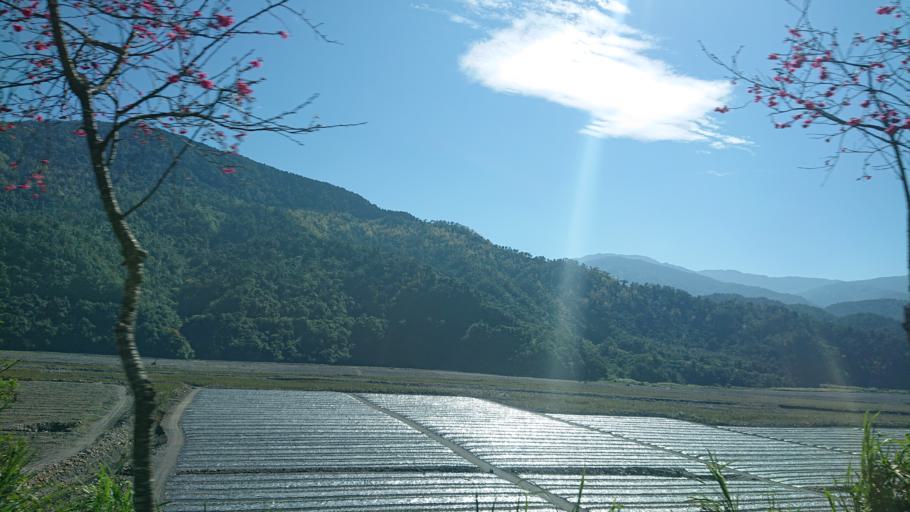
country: TW
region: Taiwan
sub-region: Yilan
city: Yilan
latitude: 24.5881
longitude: 121.5041
